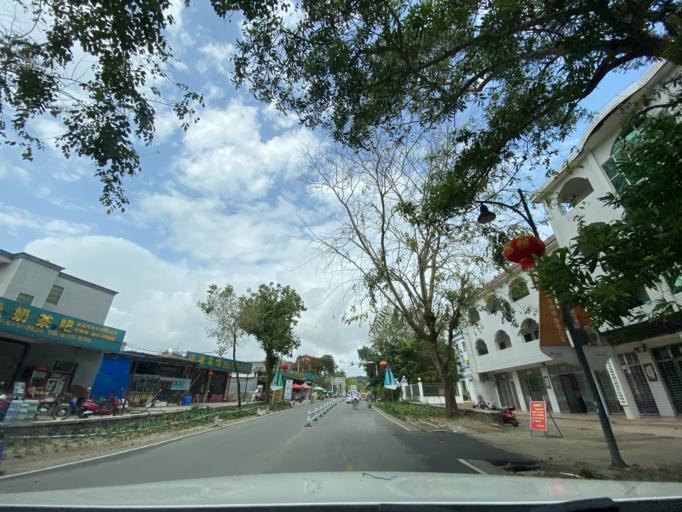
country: CN
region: Hainan
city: Liji
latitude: 18.6680
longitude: 110.2632
